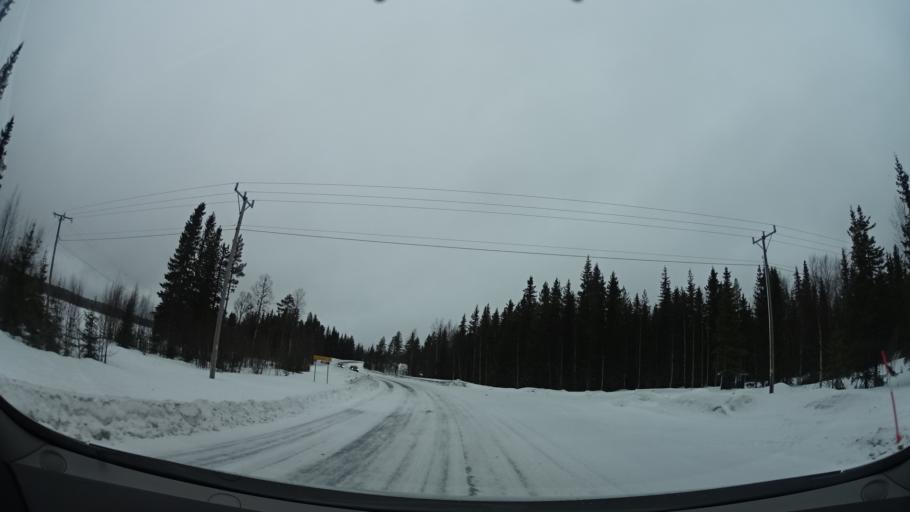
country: SE
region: Vaesterbotten
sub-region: Mala Kommun
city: Mala
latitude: 65.0851
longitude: 18.9780
